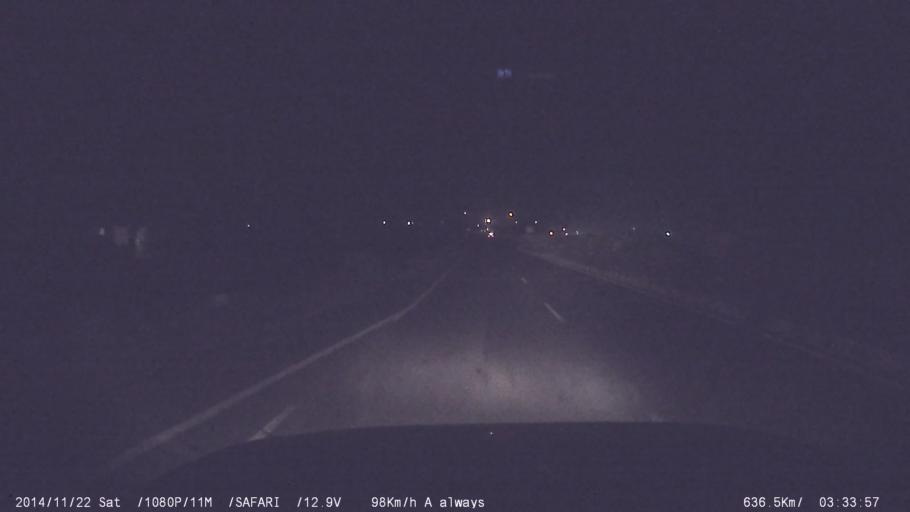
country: IN
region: Tamil Nadu
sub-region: Salem
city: Konganapuram
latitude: 11.4921
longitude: 77.8942
